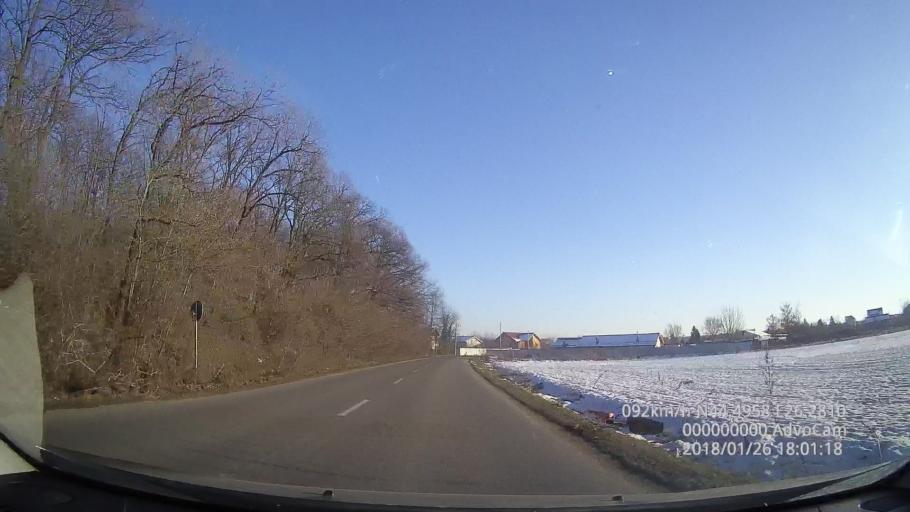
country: RO
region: Ilfov
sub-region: Comuna Ganeasa
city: Ganeasa
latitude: 44.4953
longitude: 26.2818
